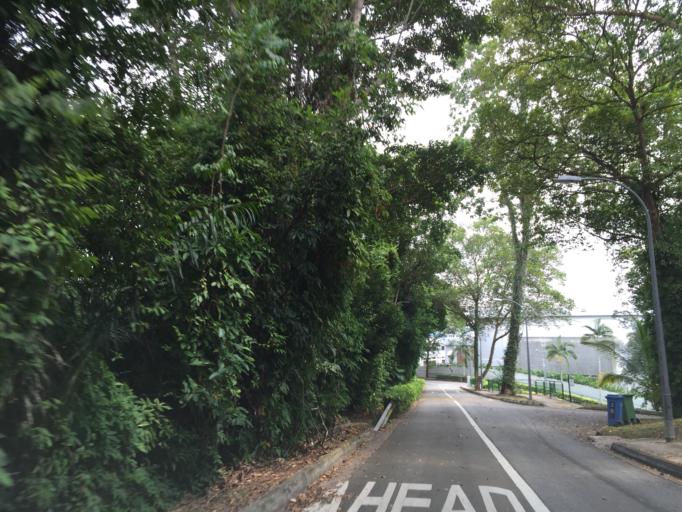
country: SG
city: Singapore
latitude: 1.3239
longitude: 103.8303
